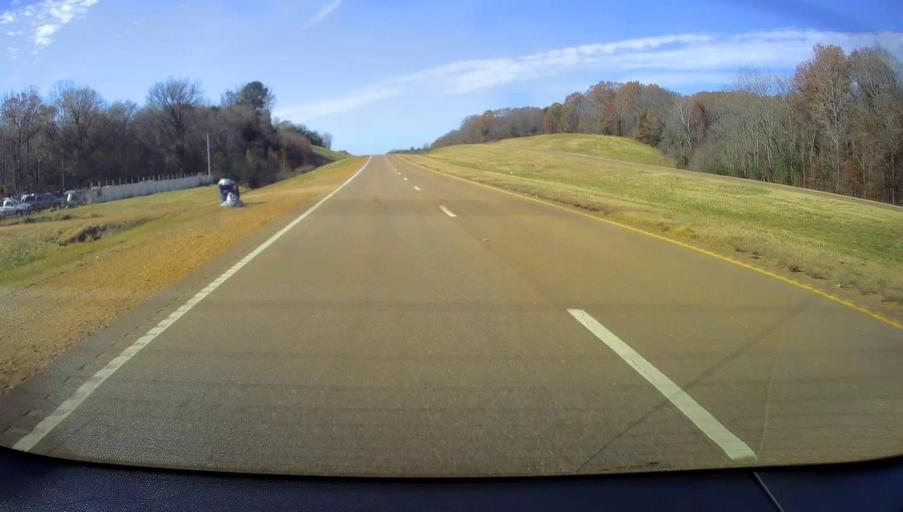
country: US
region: Mississippi
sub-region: Benton County
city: Ashland
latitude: 34.9458
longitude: -89.3337
